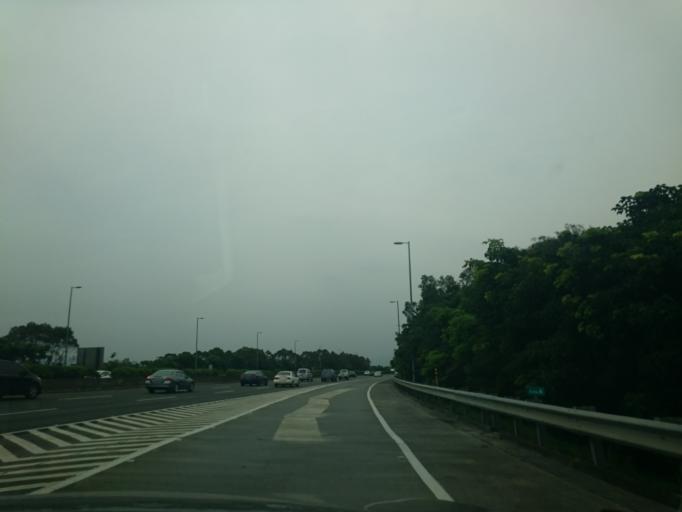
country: TW
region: Taiwan
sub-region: Nantou
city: Nantou
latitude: 23.8561
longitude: 120.7022
